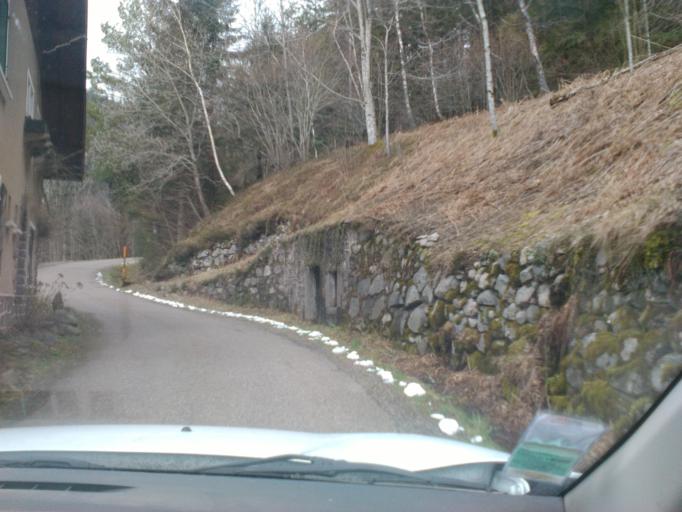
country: FR
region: Lorraine
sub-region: Departement des Vosges
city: Bussang
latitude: 47.8909
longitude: 6.8927
